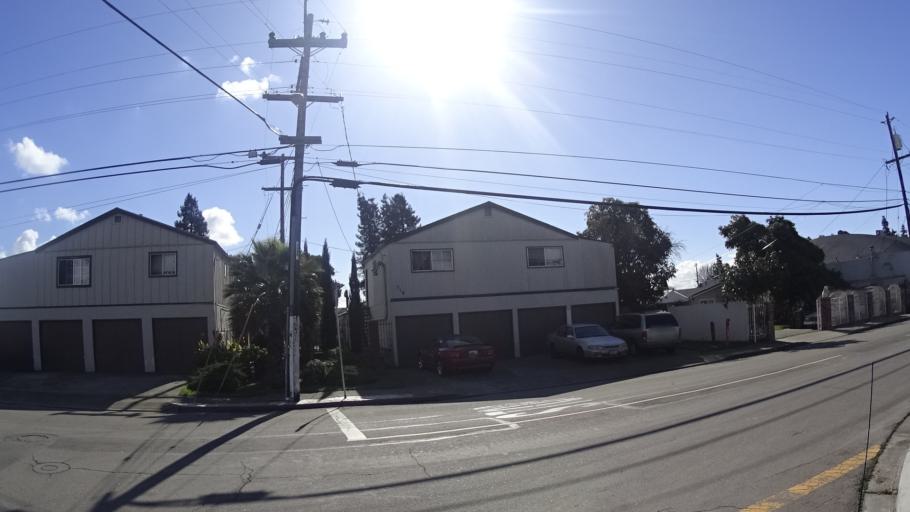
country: US
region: California
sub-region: Alameda County
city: Cherryland
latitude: 37.6609
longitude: -122.1087
